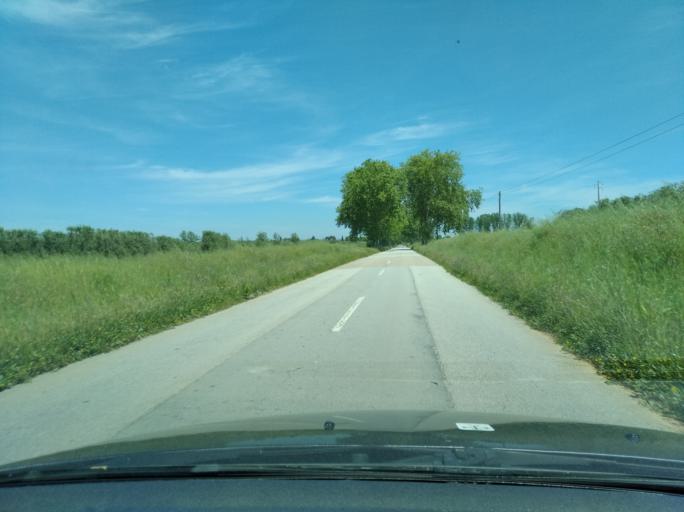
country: PT
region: Portalegre
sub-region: Avis
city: Avis
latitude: 39.0806
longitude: -7.8803
